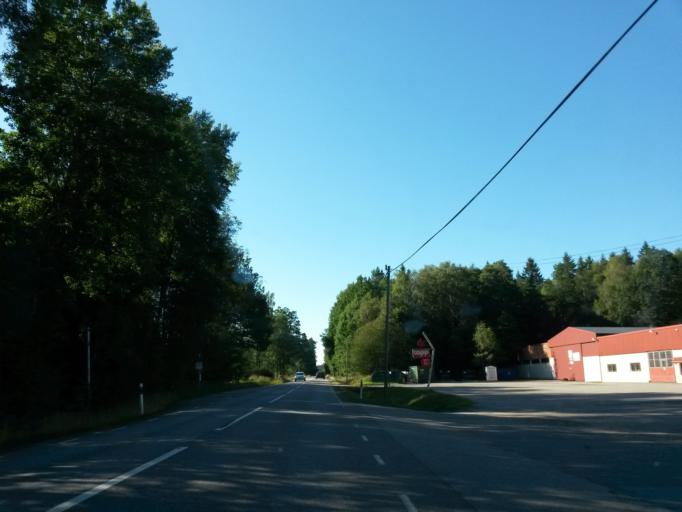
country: SE
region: Vaestra Goetaland
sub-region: Vargarda Kommun
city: Vargarda
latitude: 57.9316
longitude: 12.8558
